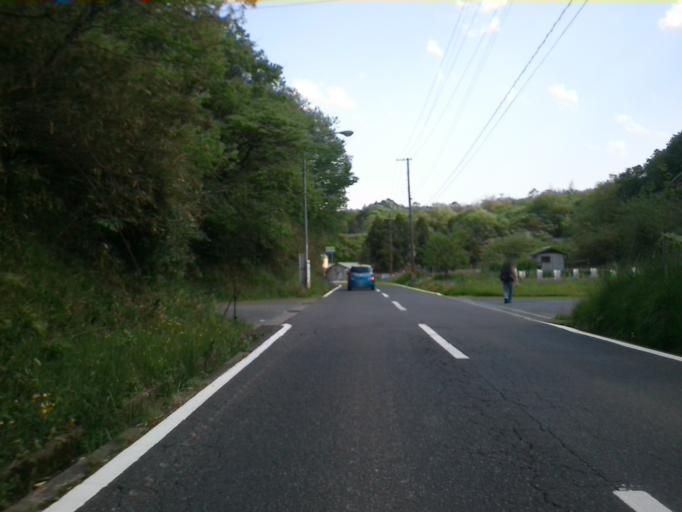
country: JP
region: Kyoto
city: Miyazu
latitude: 35.6810
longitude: 135.0679
